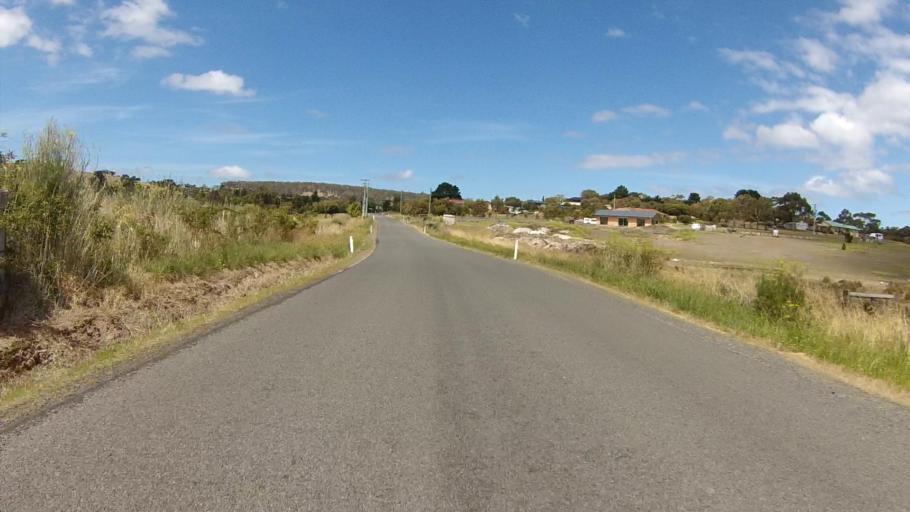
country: AU
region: Tasmania
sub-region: Sorell
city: Sorell
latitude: -42.8192
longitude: 147.6125
